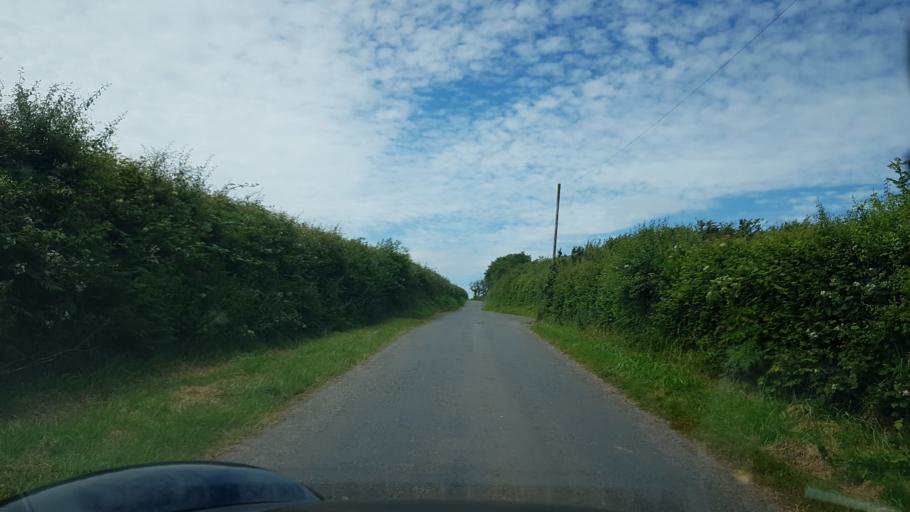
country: GB
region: Wales
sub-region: Carmarthenshire
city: Llanddowror
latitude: 51.7679
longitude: -4.5241
